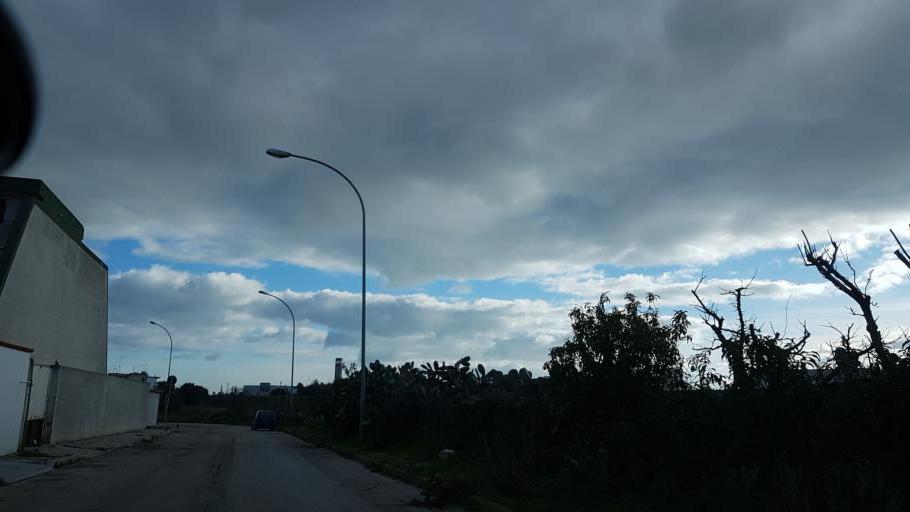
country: IT
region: Apulia
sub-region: Provincia di Brindisi
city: La Rosa
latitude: 40.6262
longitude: 17.9564
